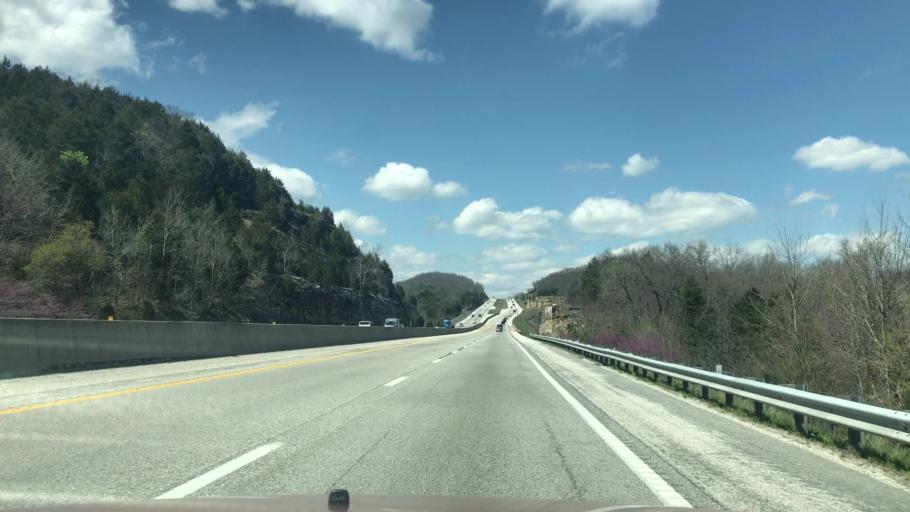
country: US
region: Missouri
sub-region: Taney County
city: Merriam Woods
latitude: 36.8605
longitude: -93.2270
